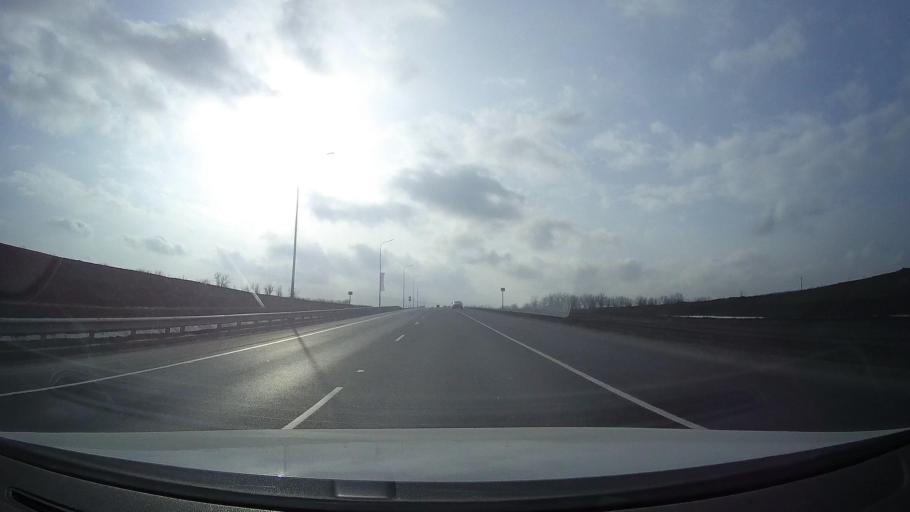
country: RU
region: Rostov
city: Grushevskaya
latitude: 47.4305
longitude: 39.8677
